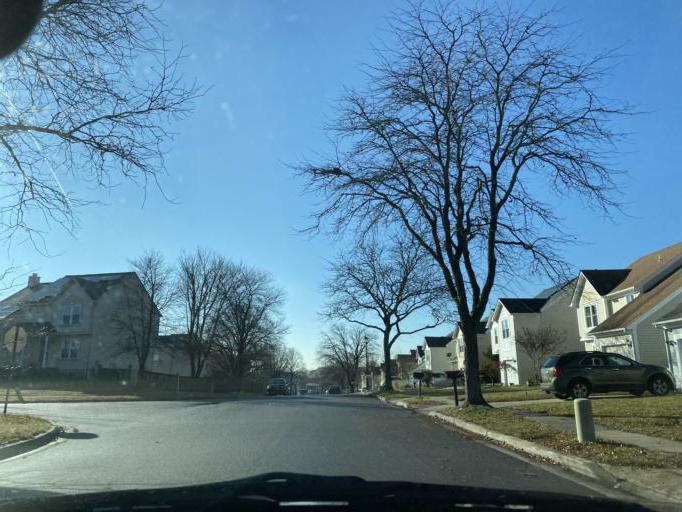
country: US
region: Maryland
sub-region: Prince George's County
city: South Laurel
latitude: 39.0836
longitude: -76.8710
